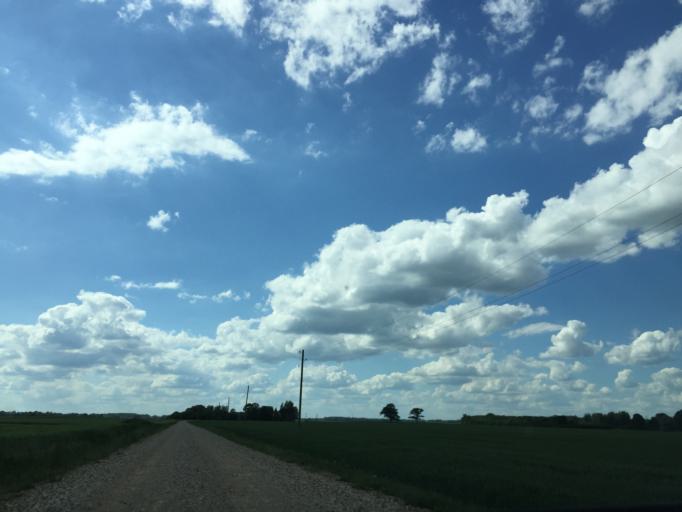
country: LV
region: Engure
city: Smarde
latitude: 56.8692
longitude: 23.3570
